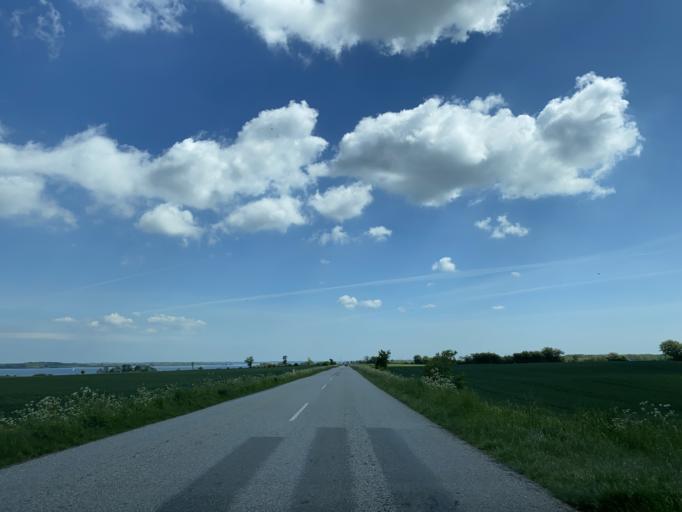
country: DK
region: South Denmark
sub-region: Sonderborg Kommune
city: Grasten
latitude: 55.0116
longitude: 9.6124
